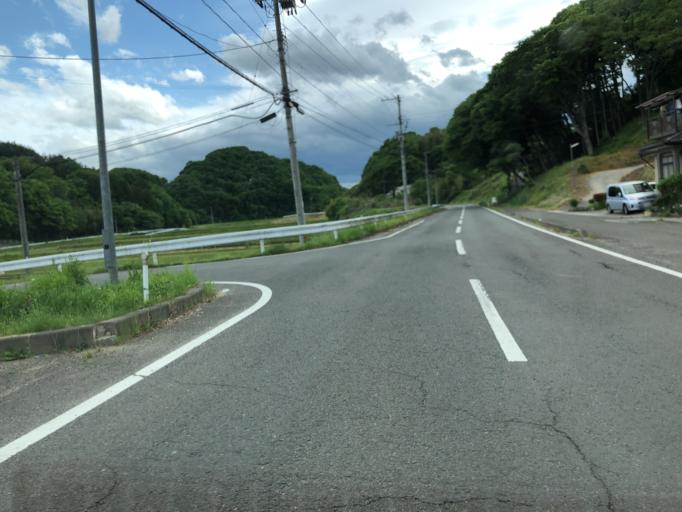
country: JP
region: Fukushima
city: Nihommatsu
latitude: 37.6390
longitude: 140.4996
